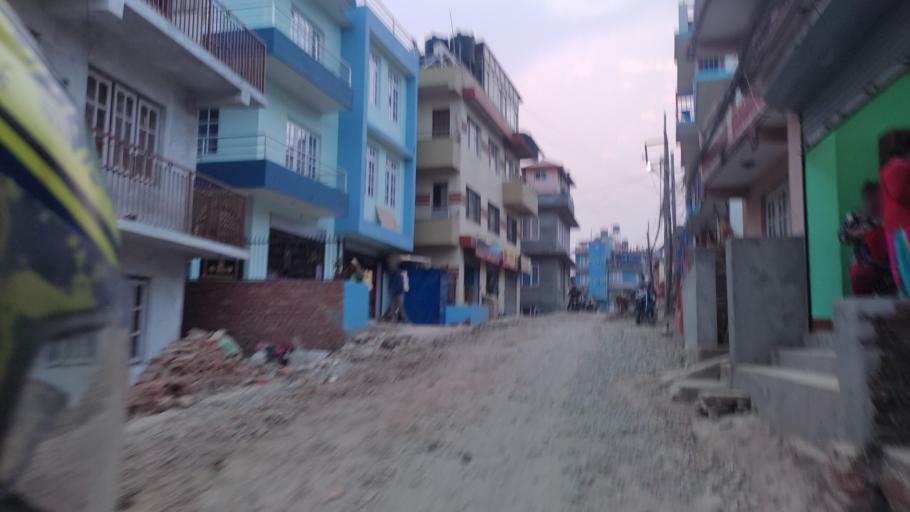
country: NP
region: Central Region
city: Kirtipur
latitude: 27.6719
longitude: 85.2846
